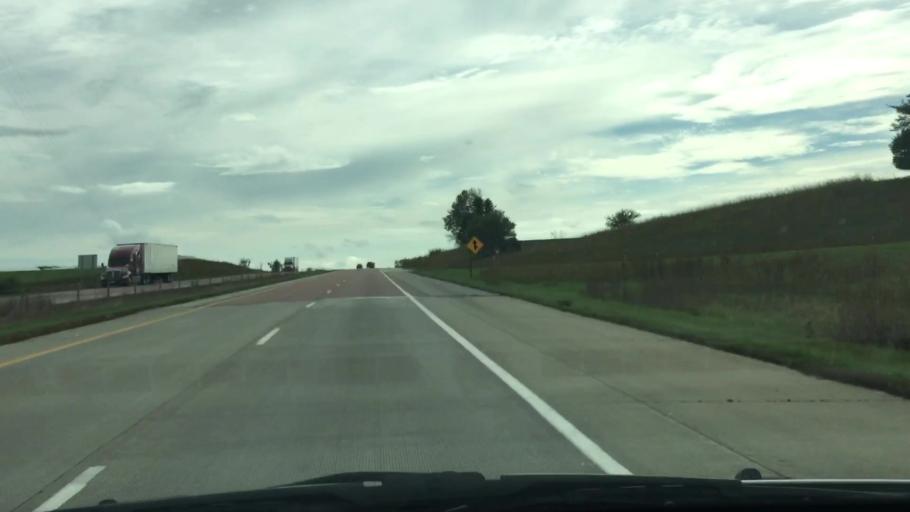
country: US
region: Iowa
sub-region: Clarke County
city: Osceola
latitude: 41.2272
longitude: -93.7817
